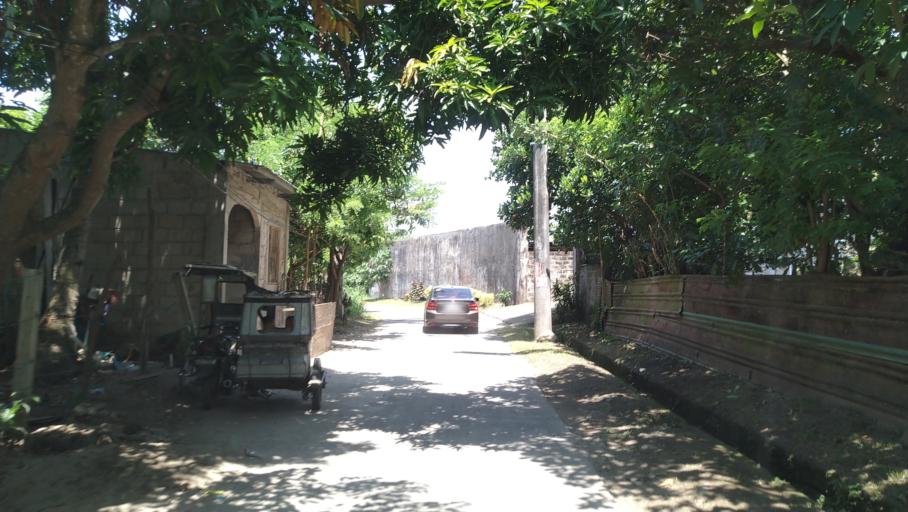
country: PH
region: Calabarzon
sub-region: Province of Laguna
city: Cabanbanan
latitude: 14.2504
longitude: 121.4142
